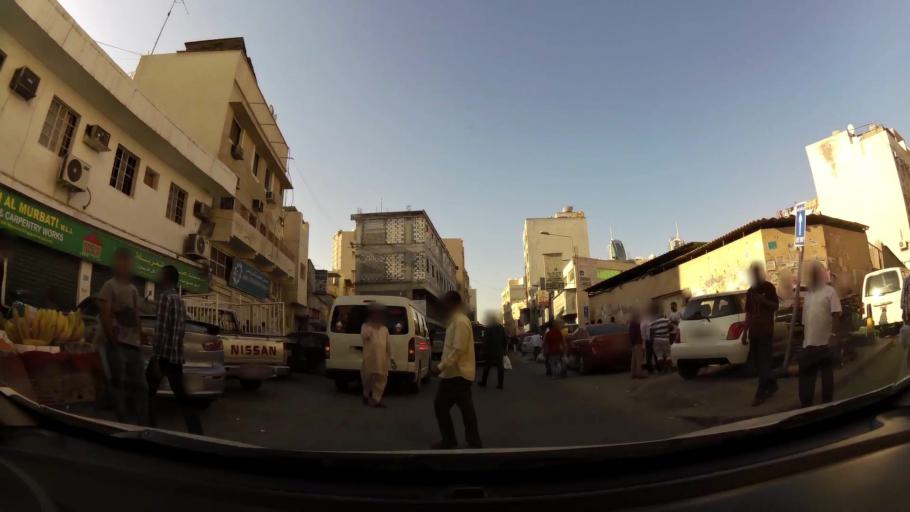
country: BH
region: Manama
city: Manama
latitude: 26.2282
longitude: 50.5716
